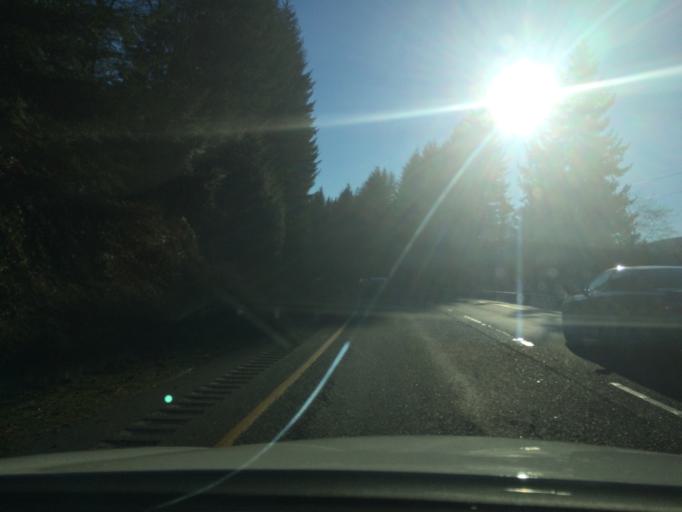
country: US
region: Washington
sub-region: Whatcom County
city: Sudden Valley
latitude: 48.6783
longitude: -122.3947
